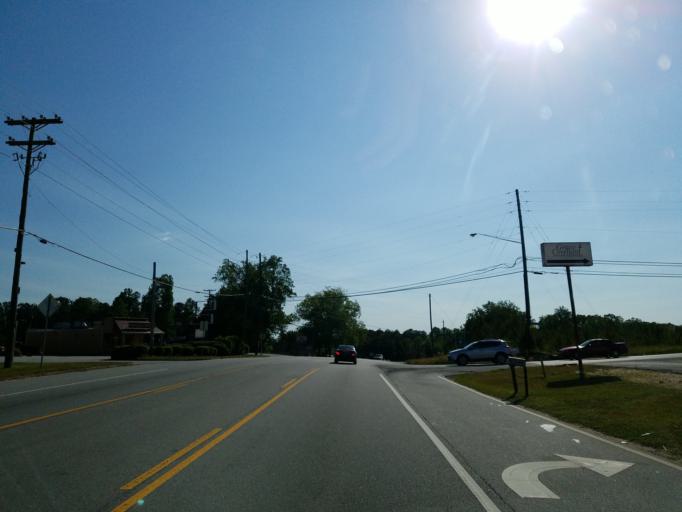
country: US
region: Georgia
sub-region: Paulding County
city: Dallas
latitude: 33.9102
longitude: -84.8048
